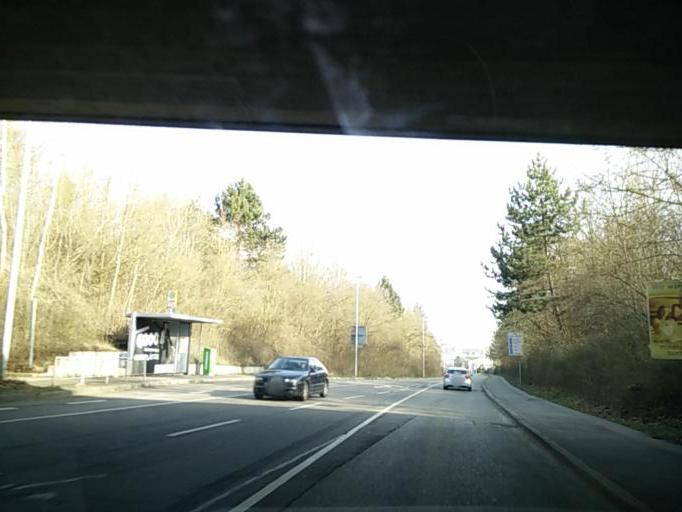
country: DE
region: Baden-Wuerttemberg
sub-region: Regierungsbezirk Stuttgart
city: Boeblingen
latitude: 48.6731
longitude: 9.0113
